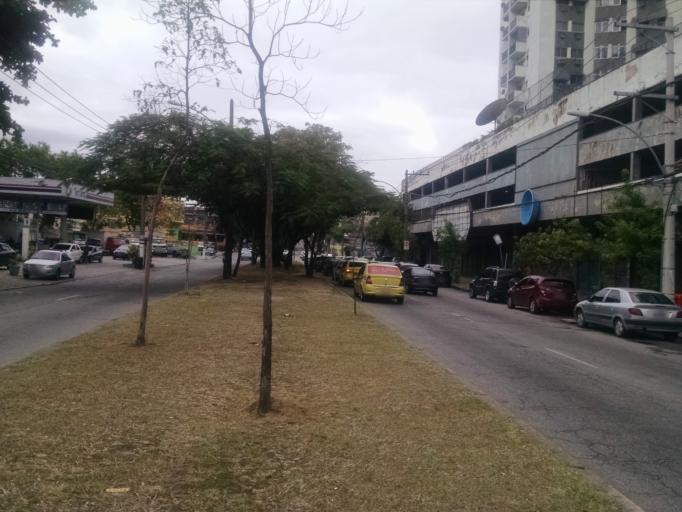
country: BR
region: Rio de Janeiro
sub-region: Duque De Caxias
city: Duque de Caxias
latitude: -22.8347
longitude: -43.3089
